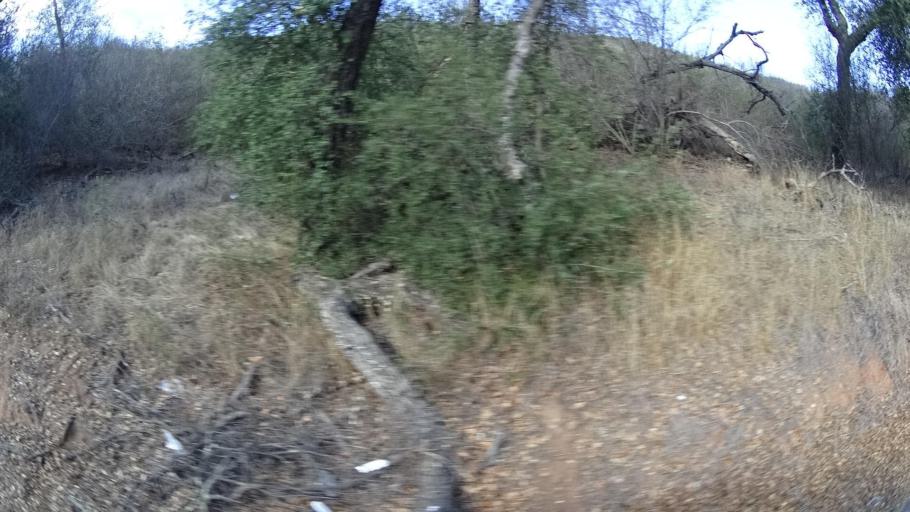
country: US
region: California
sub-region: San Diego County
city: Valley Center
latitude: 33.1717
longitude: -116.9679
